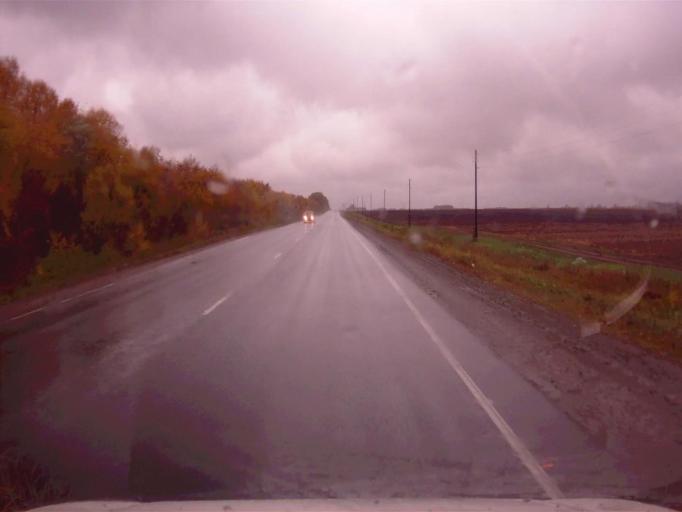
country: RU
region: Chelyabinsk
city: Argayash
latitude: 55.4264
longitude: 61.0012
